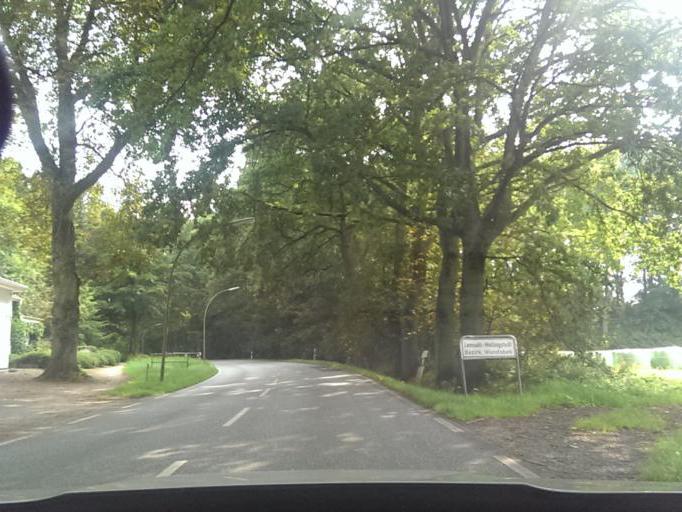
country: DE
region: Hamburg
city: Lemsahl-Mellingstedt
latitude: 53.6958
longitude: 10.0997
